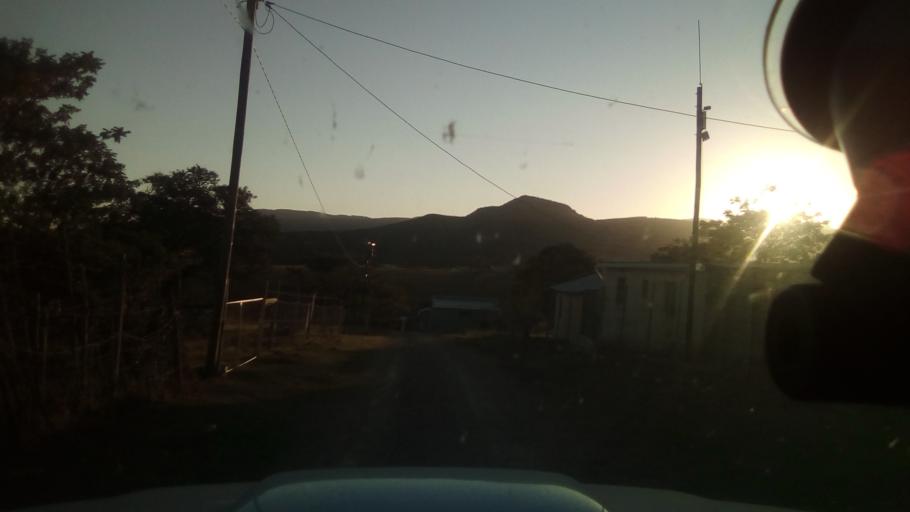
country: ZA
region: Eastern Cape
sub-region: Buffalo City Metropolitan Municipality
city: Bhisho
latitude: -32.7403
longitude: 27.3759
